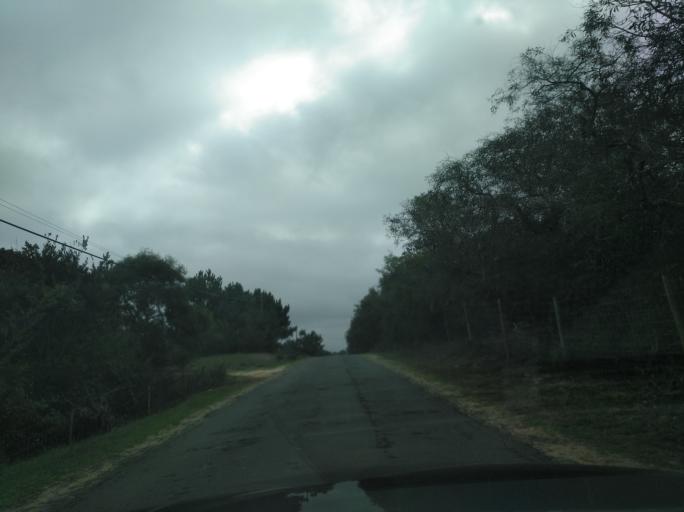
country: PT
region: Setubal
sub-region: Sines
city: Porto Covo
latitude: 37.8342
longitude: -8.7871
